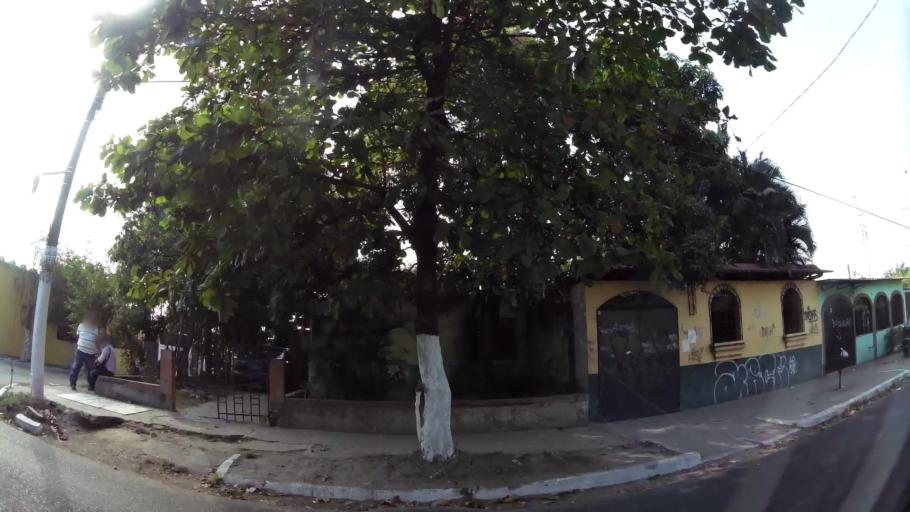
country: SV
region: San Salvador
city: Soyapango
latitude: 13.7195
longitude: -89.1273
